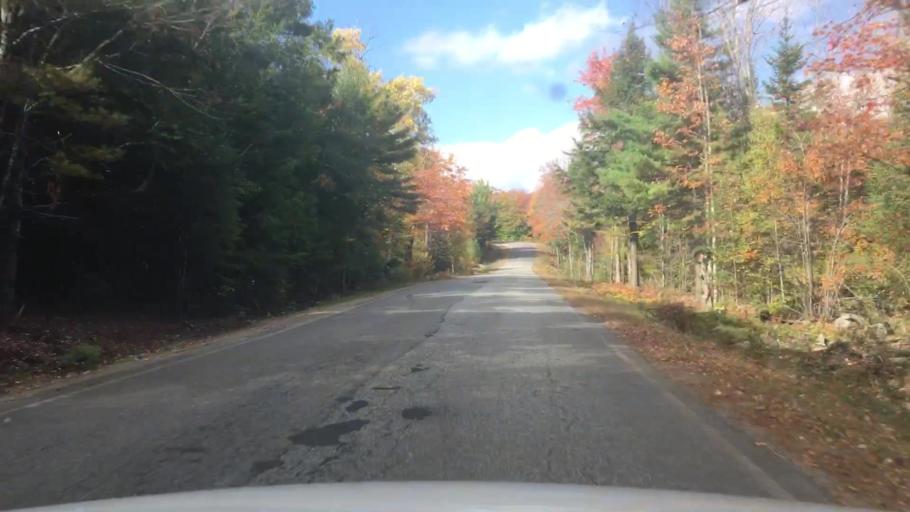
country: US
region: Maine
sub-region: Knox County
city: Washington
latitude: 44.3349
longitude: -69.3716
